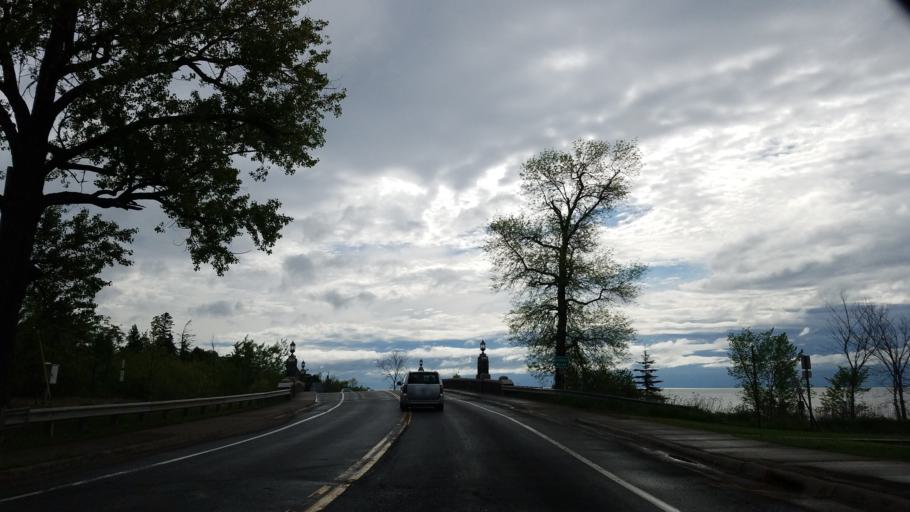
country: US
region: Minnesota
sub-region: Saint Louis County
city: Arnold
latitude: 46.8366
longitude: -92.0073
